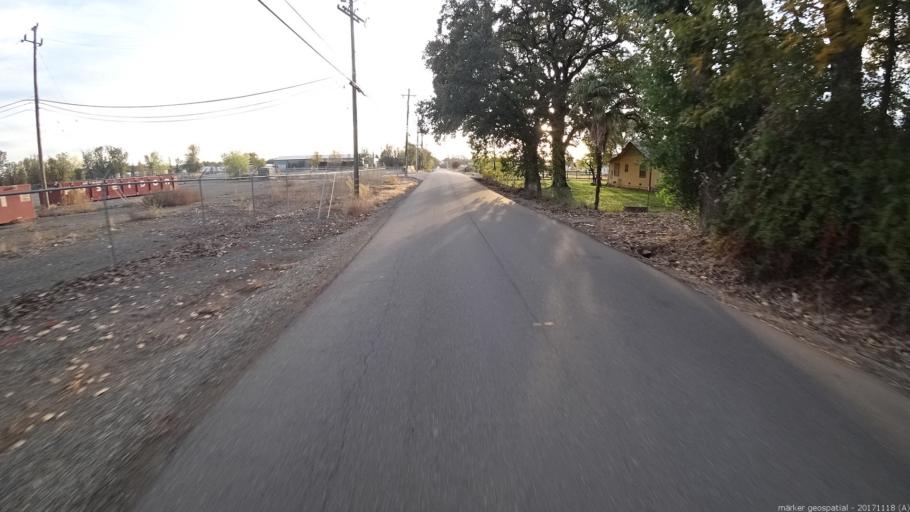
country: US
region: California
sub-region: Shasta County
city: Anderson
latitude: 40.4624
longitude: -122.3118
